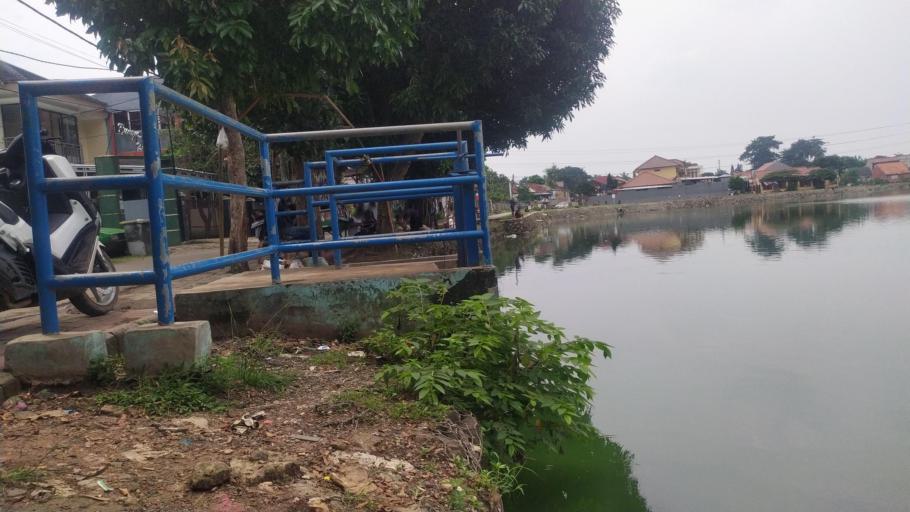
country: ID
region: Banten
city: South Tangerang
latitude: -6.2903
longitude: 106.7401
